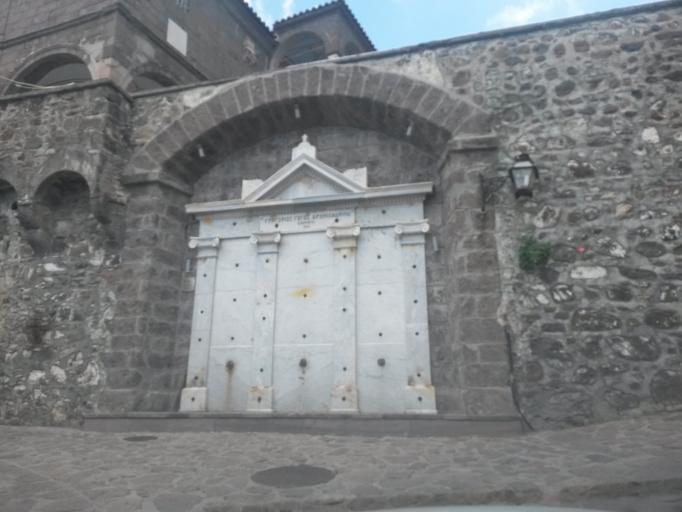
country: GR
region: North Aegean
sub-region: Nomos Lesvou
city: Eresos
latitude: 39.2255
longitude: 26.0511
